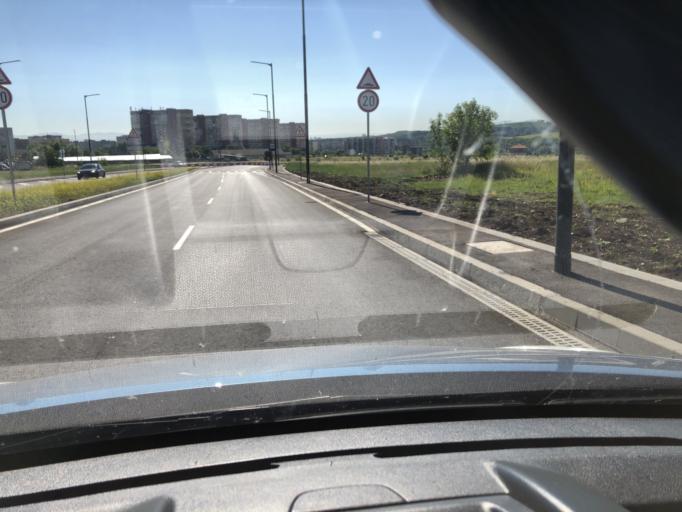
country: BG
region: Sofiya
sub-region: Obshtina Bozhurishte
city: Bozhurishte
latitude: 42.7125
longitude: 23.2346
